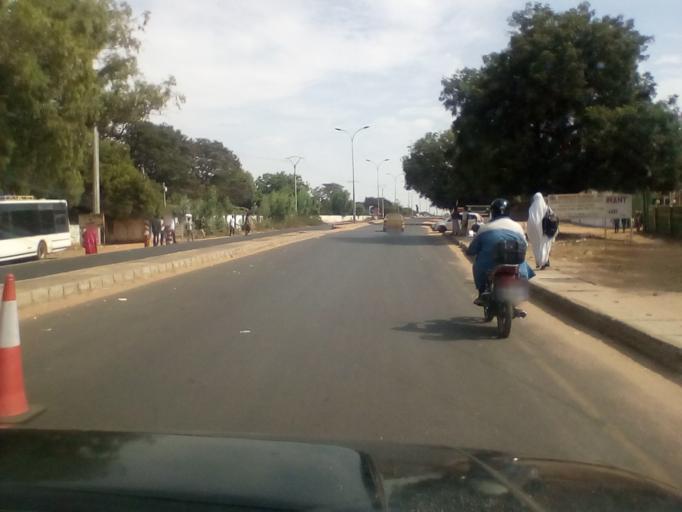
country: GM
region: Western
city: Abuko
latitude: 13.4015
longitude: -16.6548
